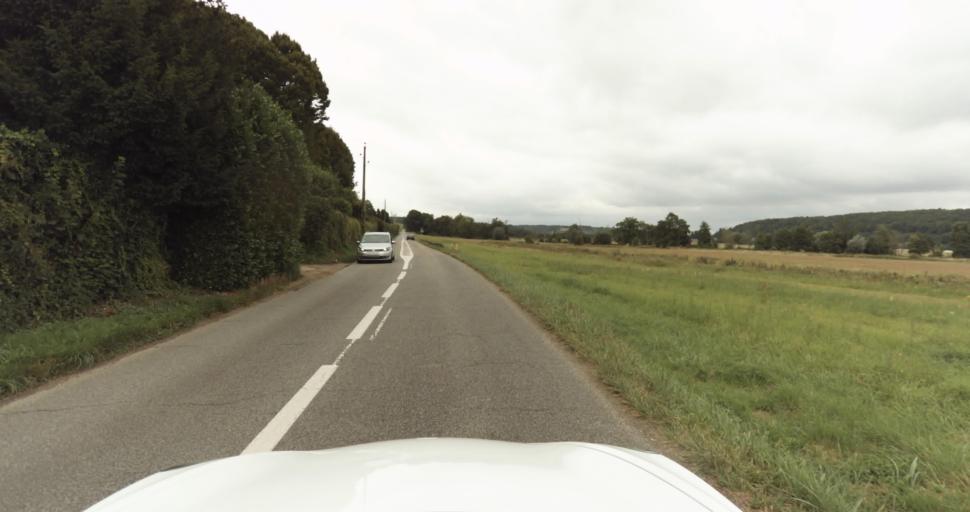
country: FR
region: Haute-Normandie
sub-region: Departement de l'Eure
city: Arnieres-sur-Iton
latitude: 49.0066
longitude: 1.1037
